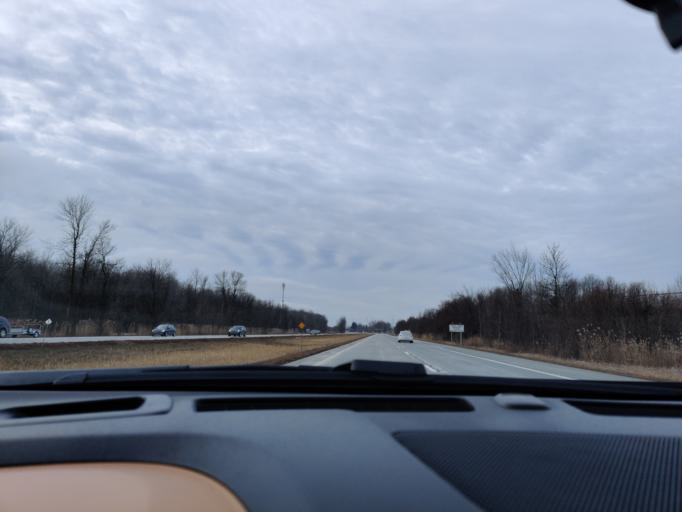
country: CA
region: Quebec
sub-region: Monteregie
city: Les Coteaux
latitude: 45.1515
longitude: -74.4728
